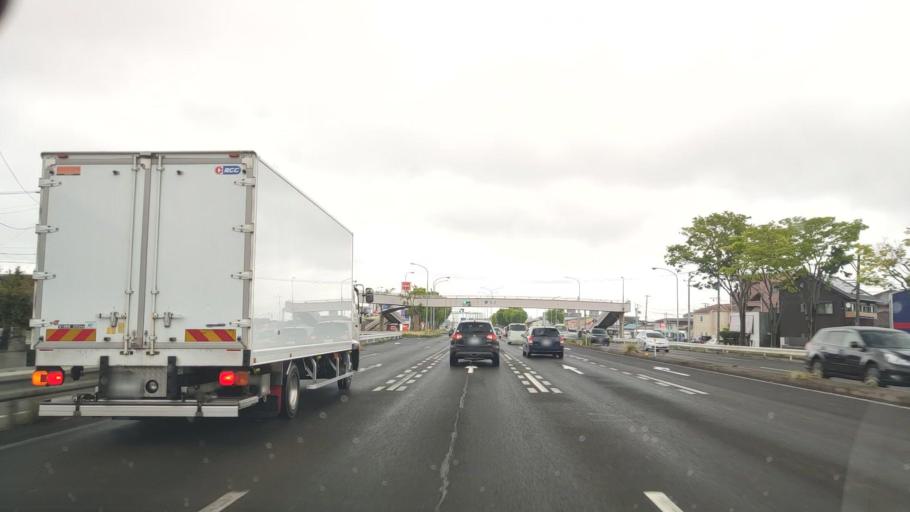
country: JP
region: Miyagi
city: Sendai
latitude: 38.2391
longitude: 140.9169
